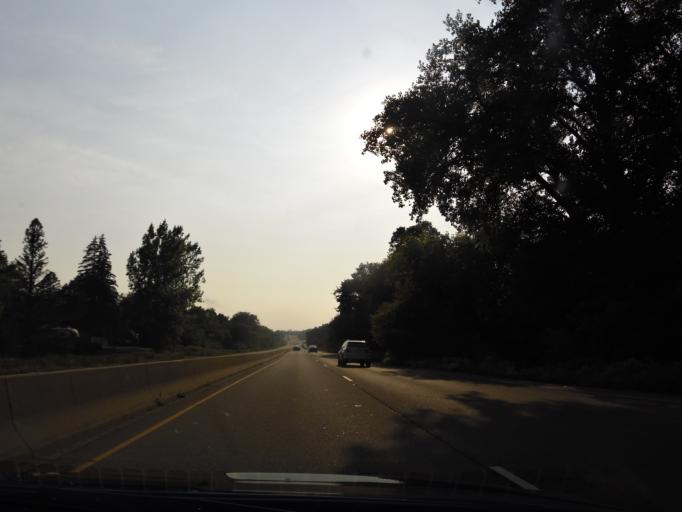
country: US
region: Minnesota
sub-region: Hennepin County
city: Minnetonka
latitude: 44.9173
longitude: -93.4933
